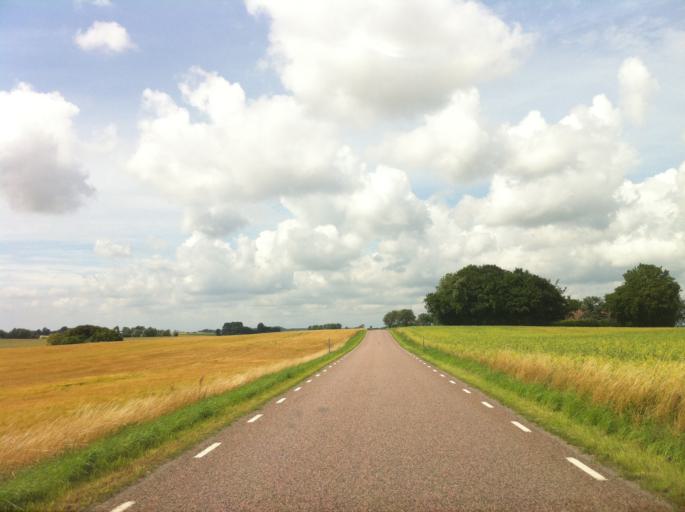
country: SE
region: Skane
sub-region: Skurups Kommun
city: Skurup
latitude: 55.4204
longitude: 13.4534
